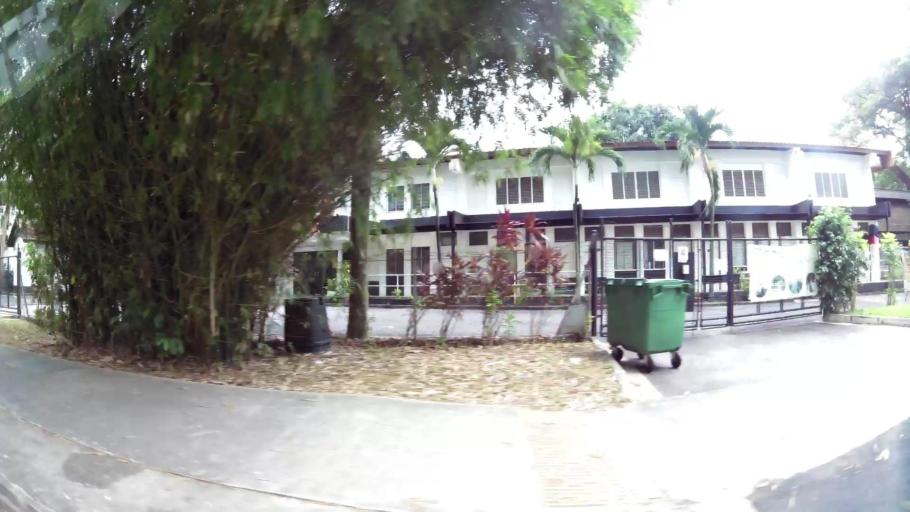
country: SG
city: Singapore
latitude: 1.3235
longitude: 103.8495
